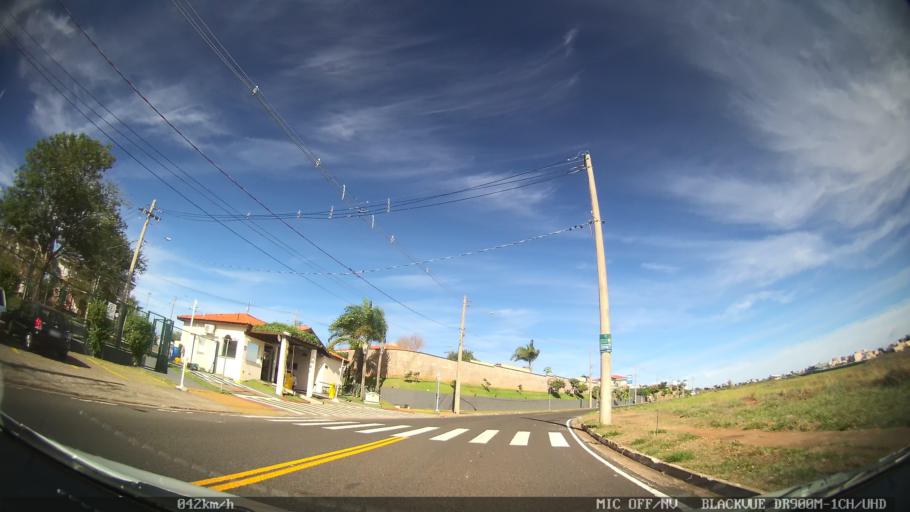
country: BR
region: Sao Paulo
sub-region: Sao Jose Do Rio Preto
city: Sao Jose do Rio Preto
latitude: -20.8016
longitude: -49.3325
